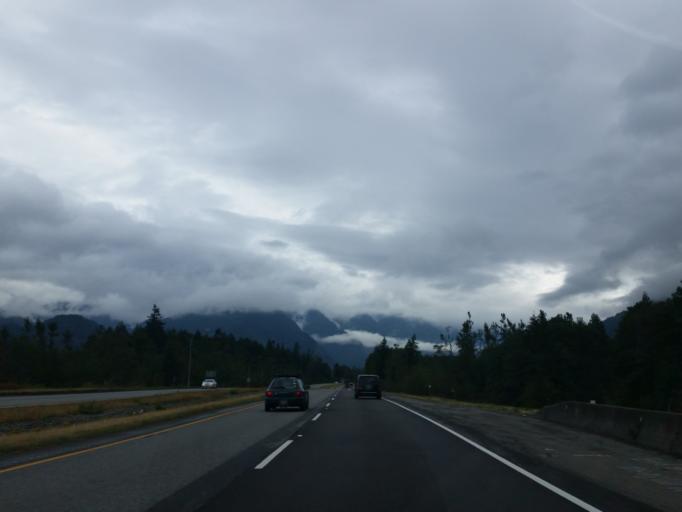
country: CA
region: British Columbia
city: Agassiz
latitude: 49.3101
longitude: -121.6350
